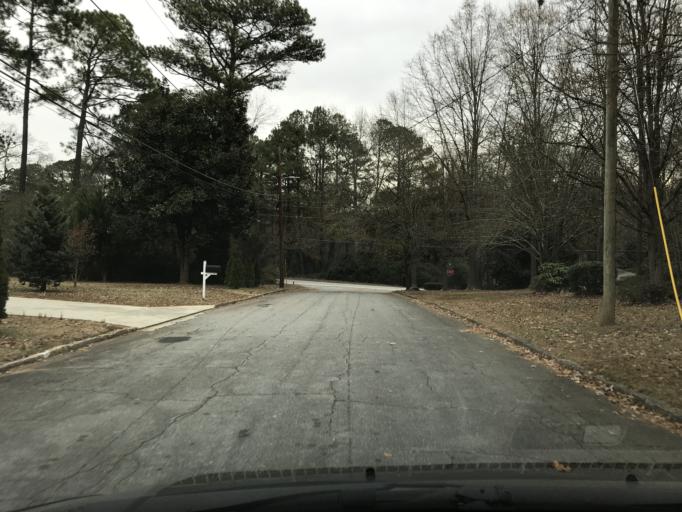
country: US
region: Georgia
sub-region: DeKalb County
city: Doraville
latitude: 33.8766
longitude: -84.2531
